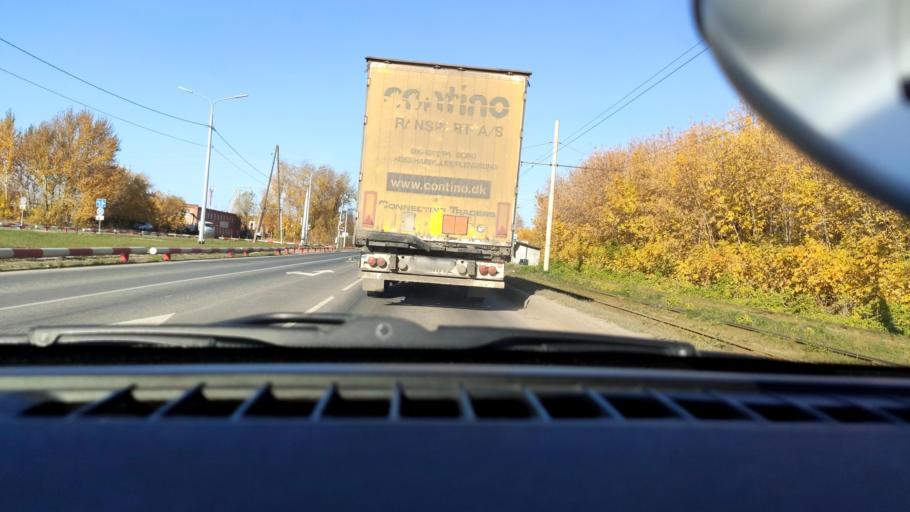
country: RU
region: Perm
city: Kondratovo
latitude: 57.9251
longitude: 56.1374
